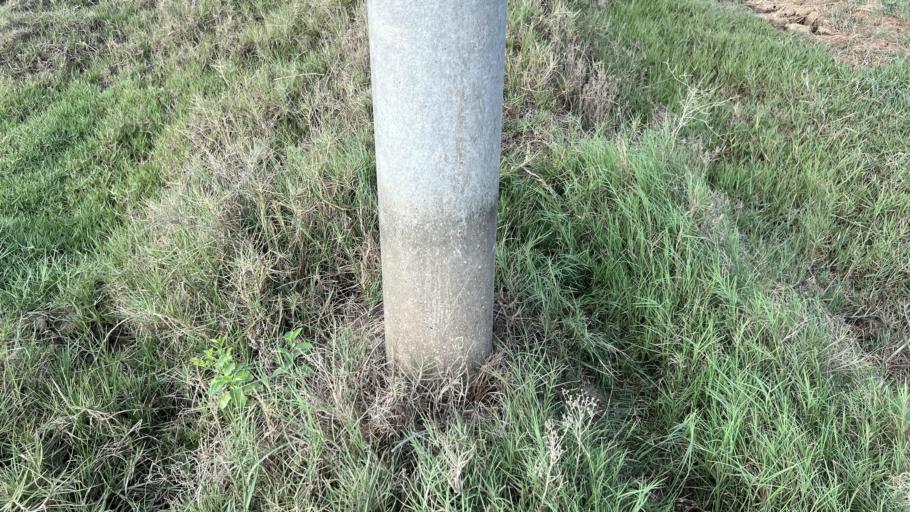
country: MM
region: Ayeyarwady
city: Pyapon
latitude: 16.1153
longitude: 95.6423
